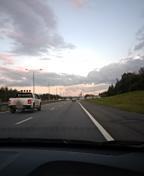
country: RU
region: Moskovskaya
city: Zhukovskiy
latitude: 55.5297
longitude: 38.1082
